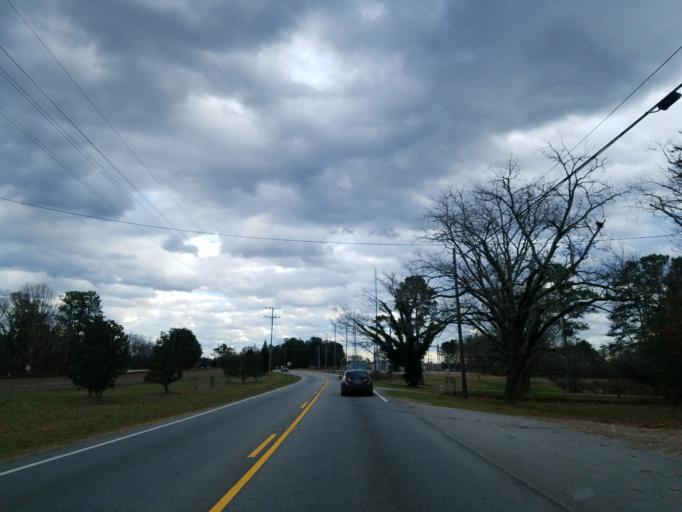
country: US
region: Georgia
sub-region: Henry County
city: Locust Grove
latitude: 33.3632
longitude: -84.1214
